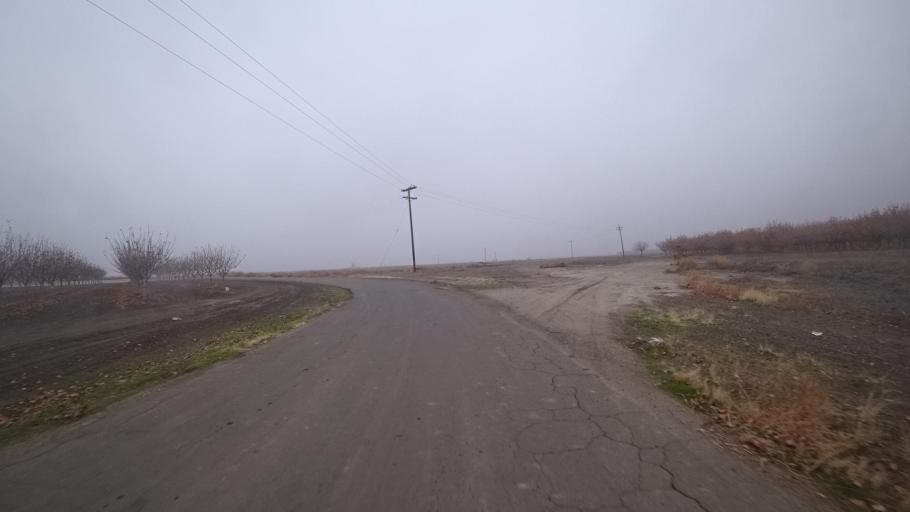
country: US
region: California
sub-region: Kern County
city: Buttonwillow
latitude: 35.4566
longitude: -119.5190
